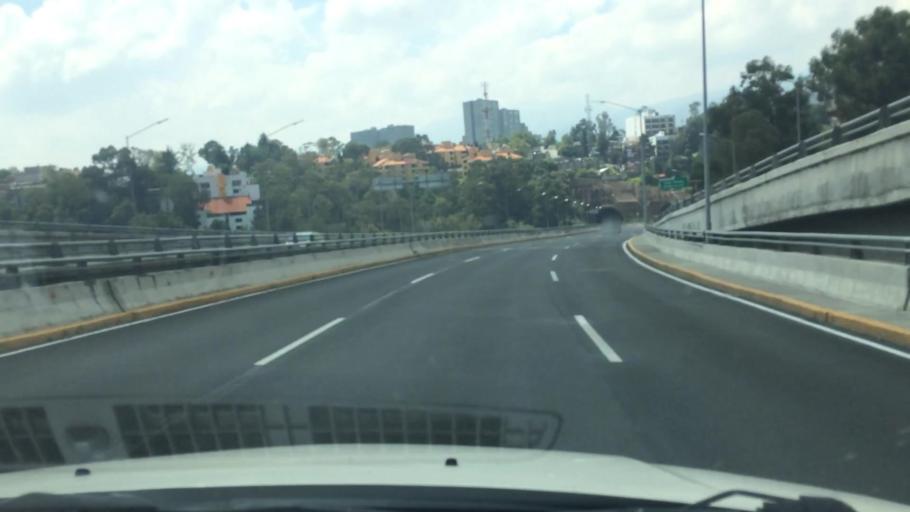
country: MX
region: Mexico City
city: Magdalena Contreras
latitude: 19.3433
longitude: -99.2395
